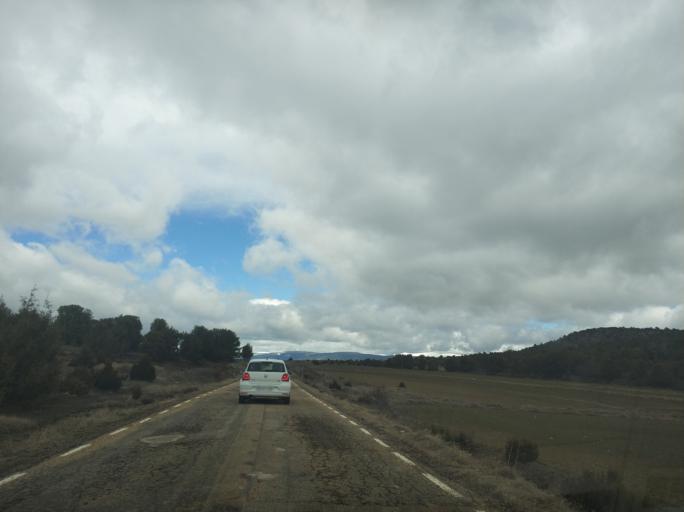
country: ES
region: Castille and Leon
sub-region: Provincia de Soria
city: Abejar
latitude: 41.7907
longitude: -2.7686
